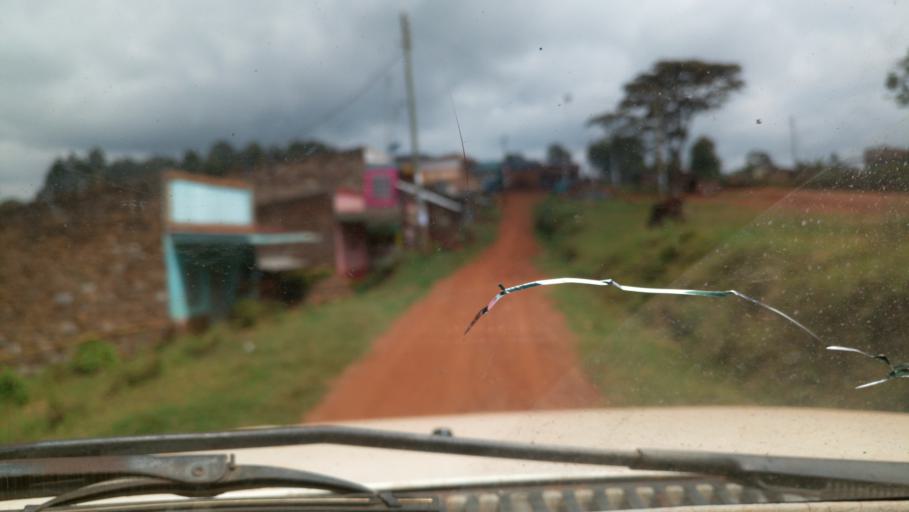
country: KE
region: Murang'a District
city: Kangema
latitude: -0.7621
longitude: 36.9063
